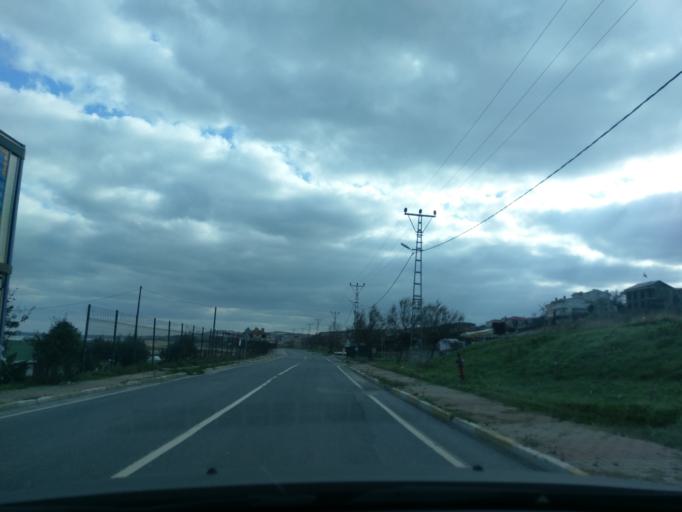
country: TR
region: Istanbul
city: Durusu
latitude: 41.3426
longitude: 28.6842
